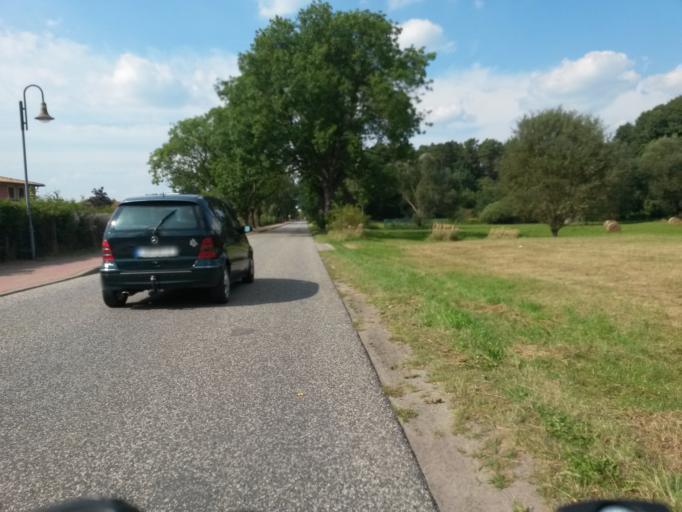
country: DE
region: Brandenburg
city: Templin
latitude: 53.1045
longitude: 13.5255
